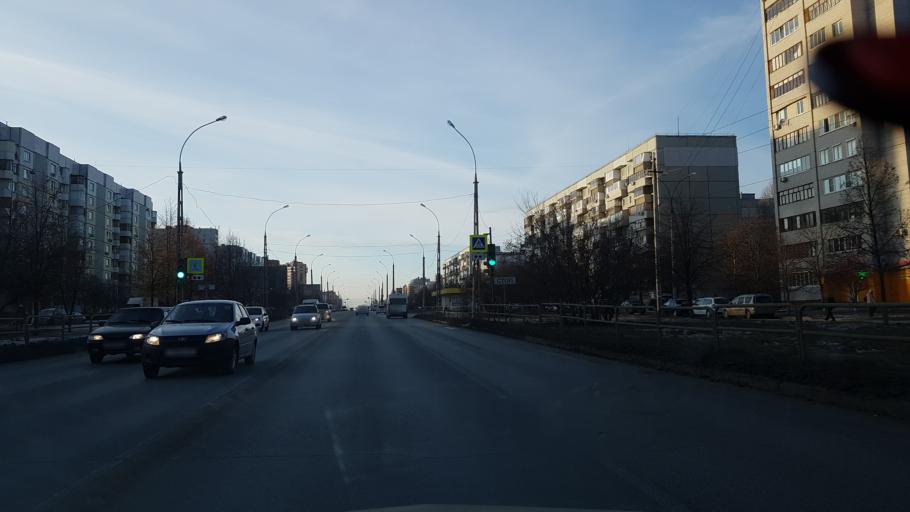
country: RU
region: Samara
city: Tol'yatti
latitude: 53.5405
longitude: 49.3527
